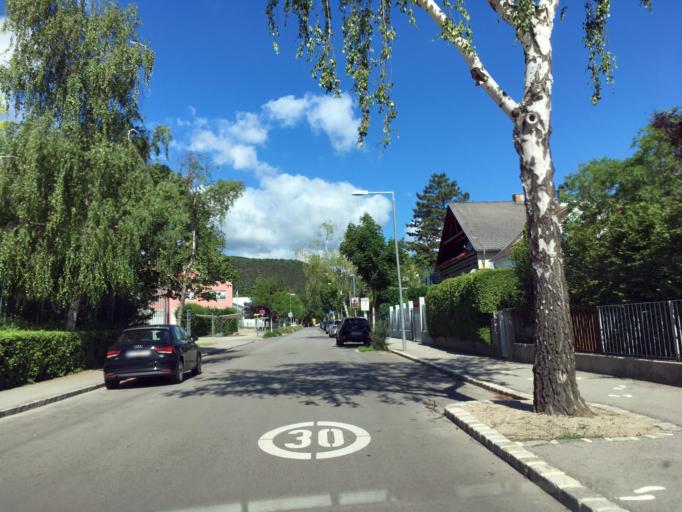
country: AT
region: Lower Austria
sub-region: Politischer Bezirk Baden
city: Baden
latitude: 48.0020
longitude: 16.2201
